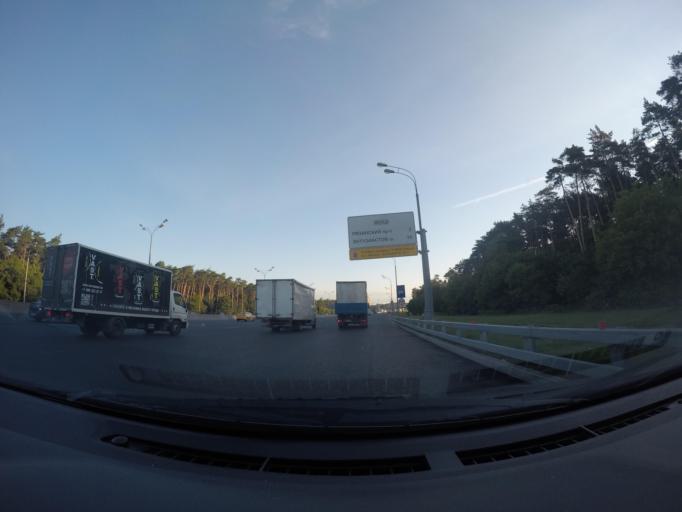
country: RU
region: Moscow
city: Vykhino-Zhulebino
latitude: 55.6905
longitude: 37.8300
